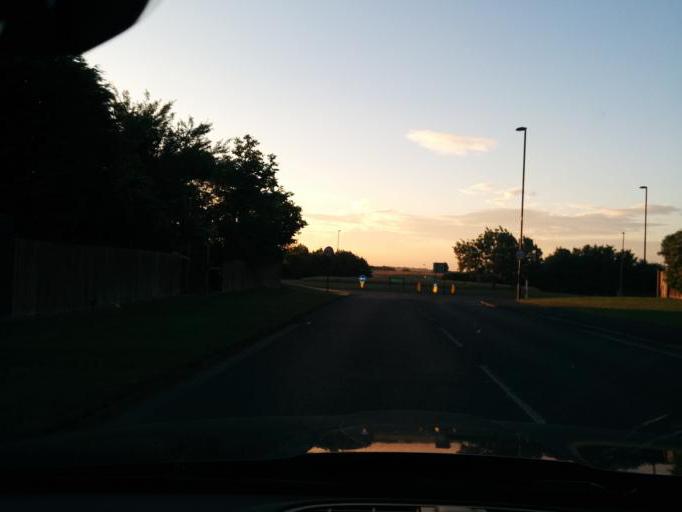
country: GB
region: England
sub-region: Northumberland
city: Seghill
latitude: 55.0415
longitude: -1.5643
